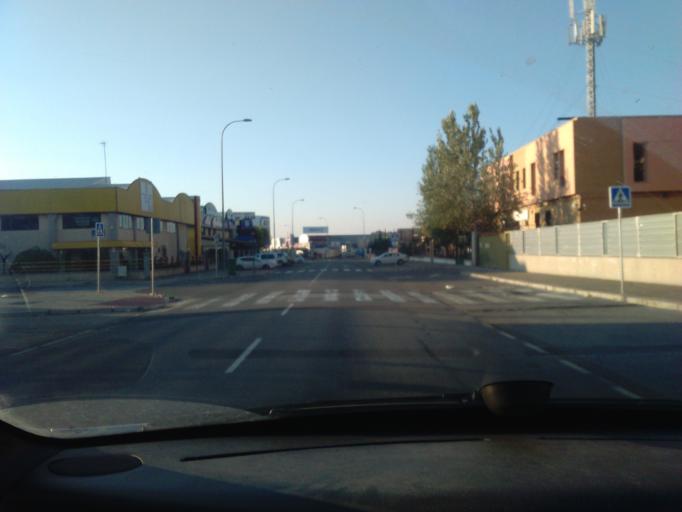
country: ES
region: Andalusia
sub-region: Provincia de Sevilla
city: Sevilla
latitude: 37.3895
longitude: -5.9455
